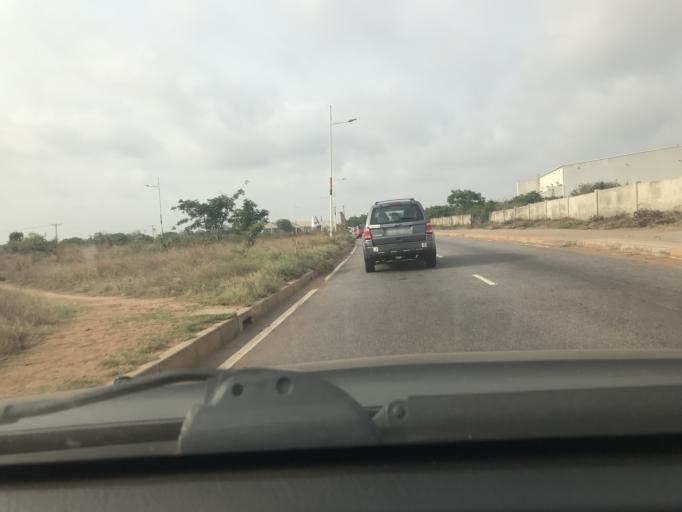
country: GH
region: Greater Accra
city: Medina Estates
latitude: 5.6067
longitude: -0.1621
